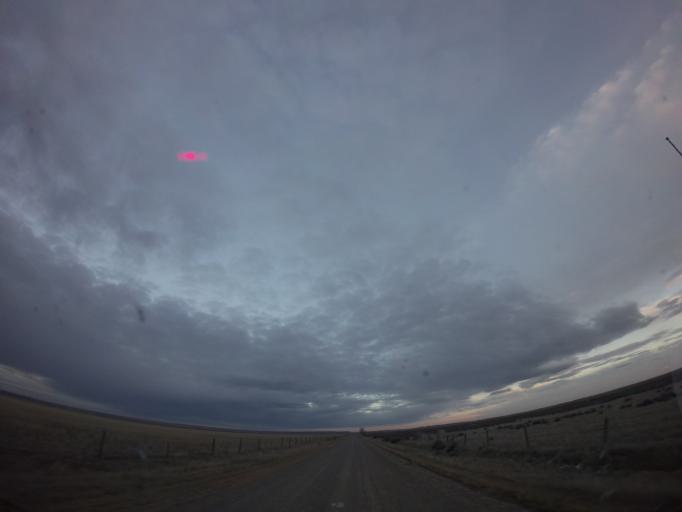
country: US
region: Montana
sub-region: Yellowstone County
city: Laurel
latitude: 45.9440
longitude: -108.7920
